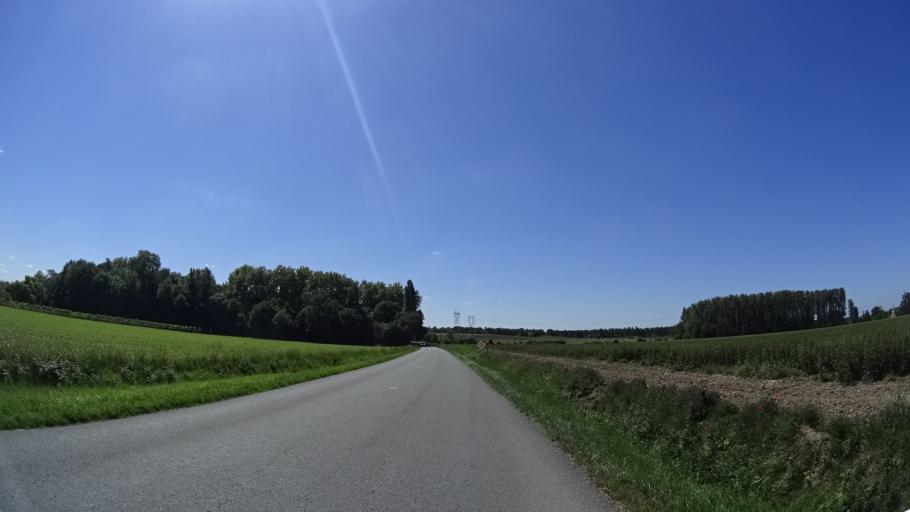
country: FR
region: Pays de la Loire
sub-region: Departement de Maine-et-Loire
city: Doue-la-Fontaine
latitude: 47.2310
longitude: -0.2784
